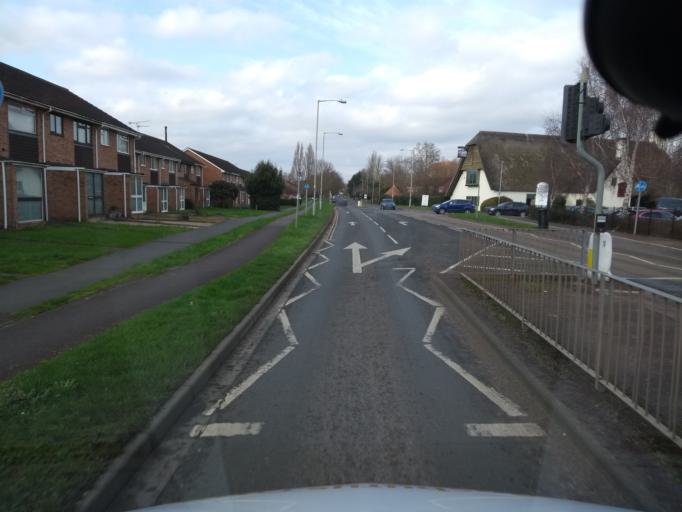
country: GB
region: England
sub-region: Somerset
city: Taunton
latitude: 51.0131
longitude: -3.0774
